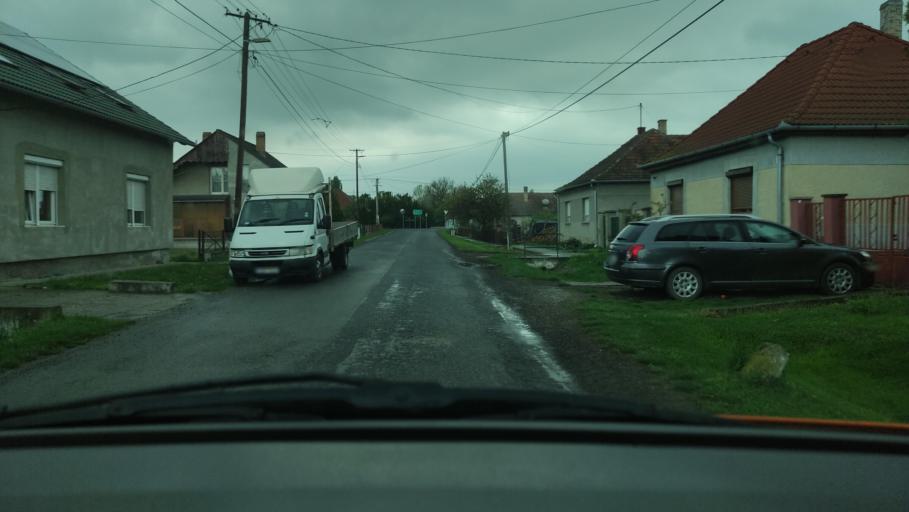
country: HU
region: Baranya
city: Mohacs
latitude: 45.9466
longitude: 18.7025
